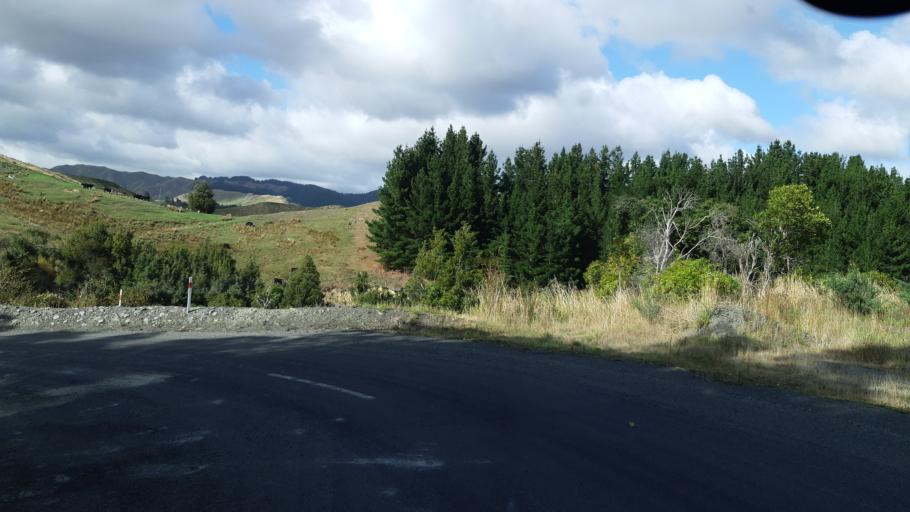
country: NZ
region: Manawatu-Wanganui
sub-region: Ruapehu District
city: Waiouru
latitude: -39.7478
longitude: 175.6631
